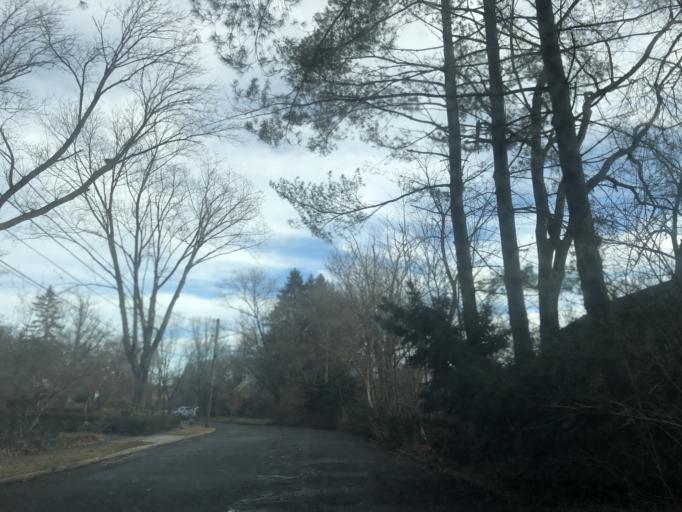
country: US
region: New Jersey
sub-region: Mercer County
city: Princeton
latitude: 40.3545
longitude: -74.6402
